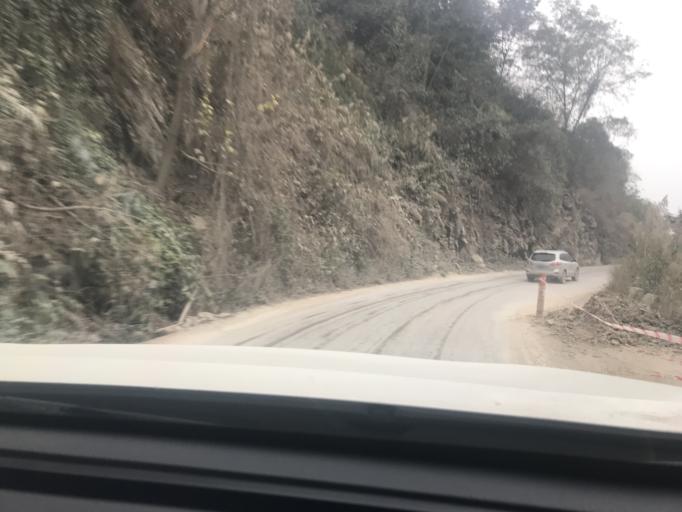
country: CN
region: Guangxi Zhuangzu Zizhiqu
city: Xinzhou
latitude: 24.9859
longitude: 105.8229
